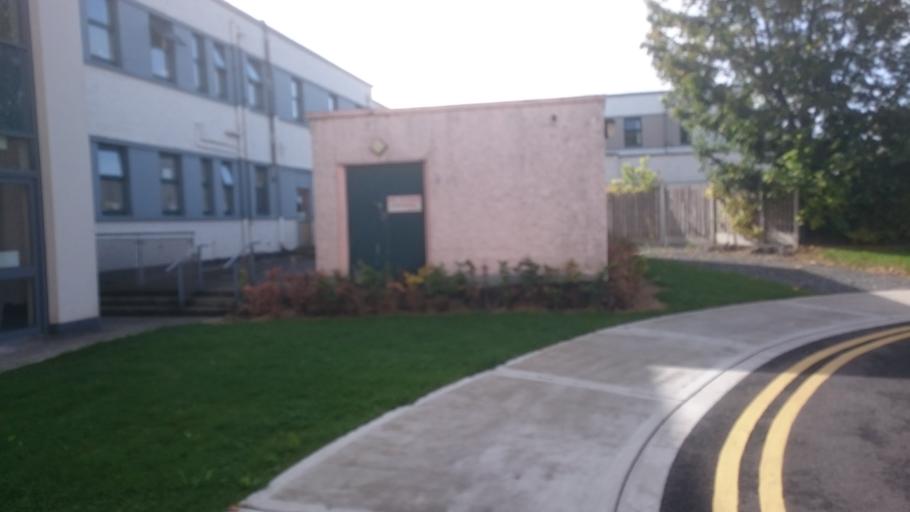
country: IE
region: Leinster
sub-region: Kilkenny
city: Kilkenny
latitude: 52.6665
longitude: -7.2641
